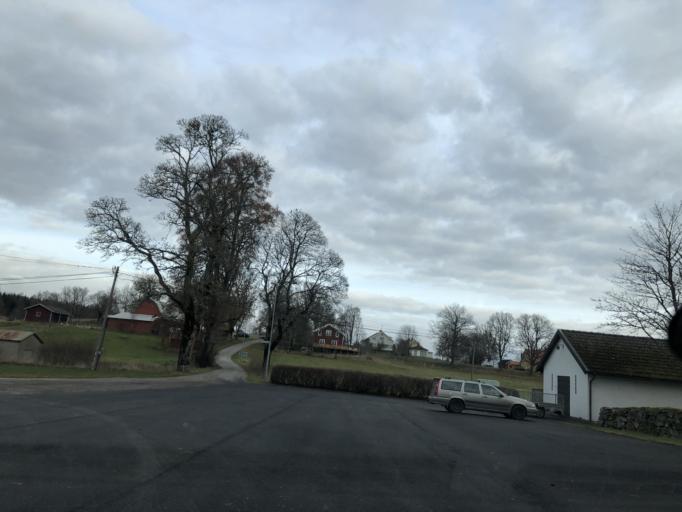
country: SE
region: Vaestra Goetaland
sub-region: Ulricehamns Kommun
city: Ulricehamn
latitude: 57.7259
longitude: 13.3134
